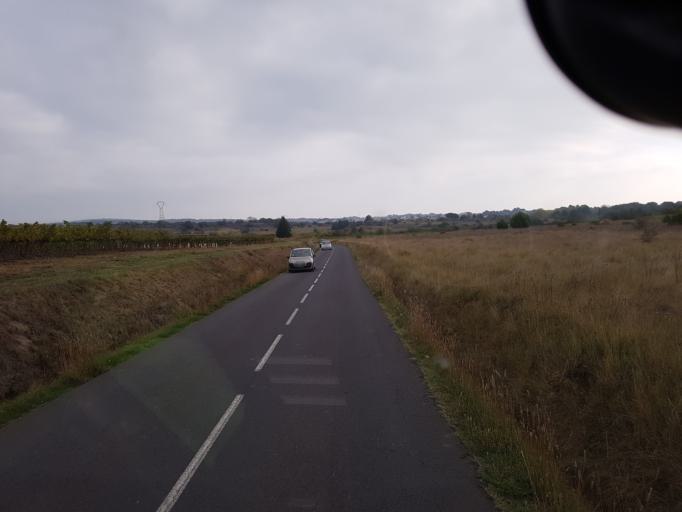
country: FR
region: Languedoc-Roussillon
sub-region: Departement de l'Herault
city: Loupian
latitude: 43.4472
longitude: 3.5896
